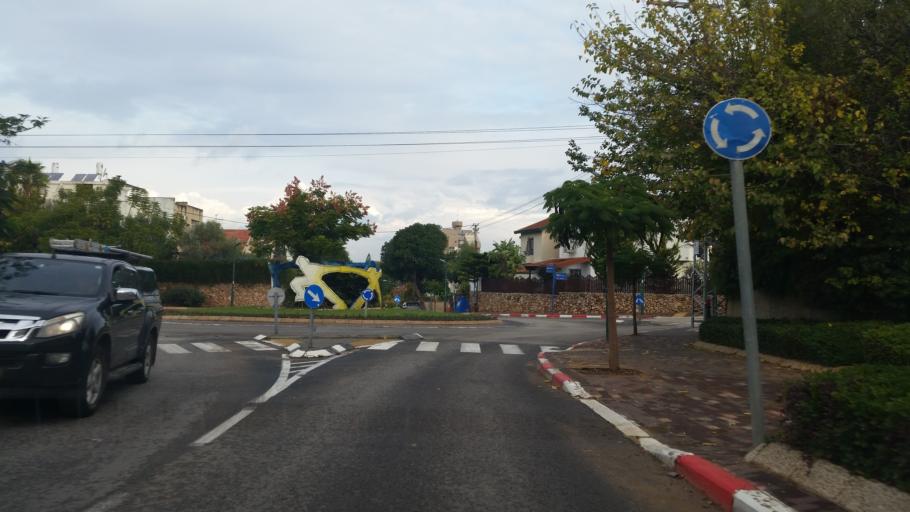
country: IL
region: Tel Aviv
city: Ramat HaSharon
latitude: 32.1562
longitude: 34.8475
